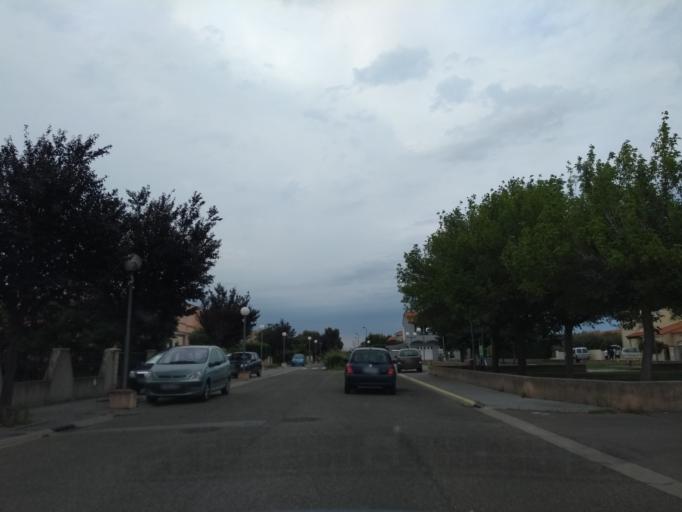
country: FR
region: Languedoc-Roussillon
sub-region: Departement des Pyrenees-Orientales
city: Elne
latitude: 42.6050
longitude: 2.9717
